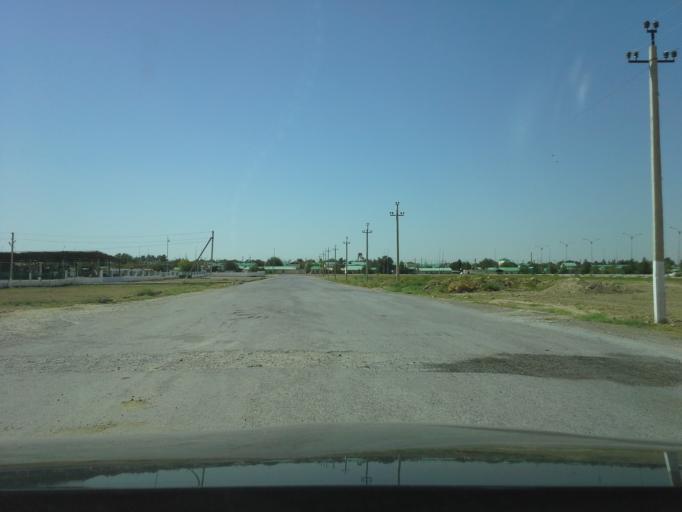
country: TM
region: Ahal
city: Ashgabat
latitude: 38.0050
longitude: 58.3091
